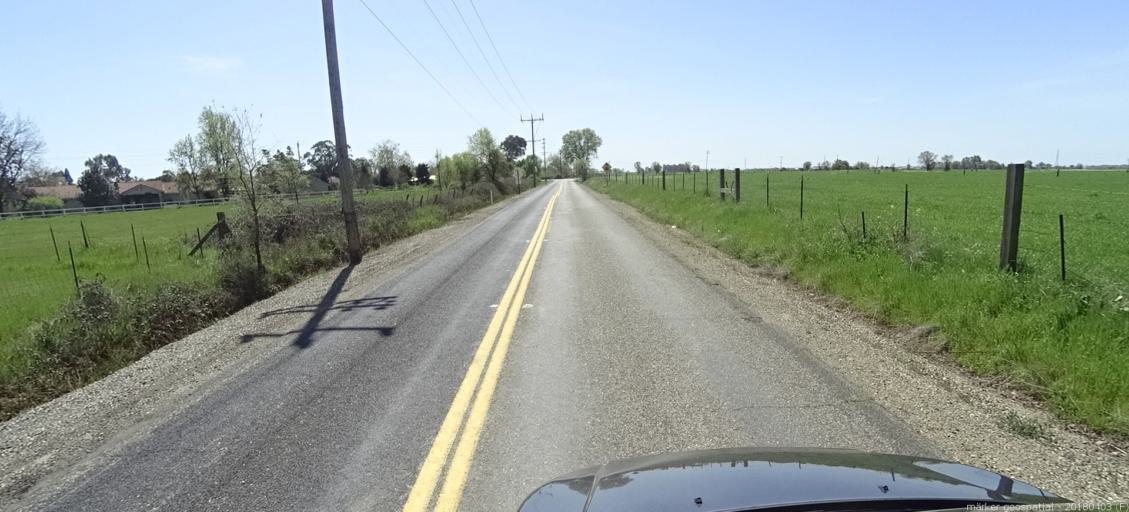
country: US
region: California
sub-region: Sacramento County
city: Wilton
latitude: 38.3933
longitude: -121.2739
